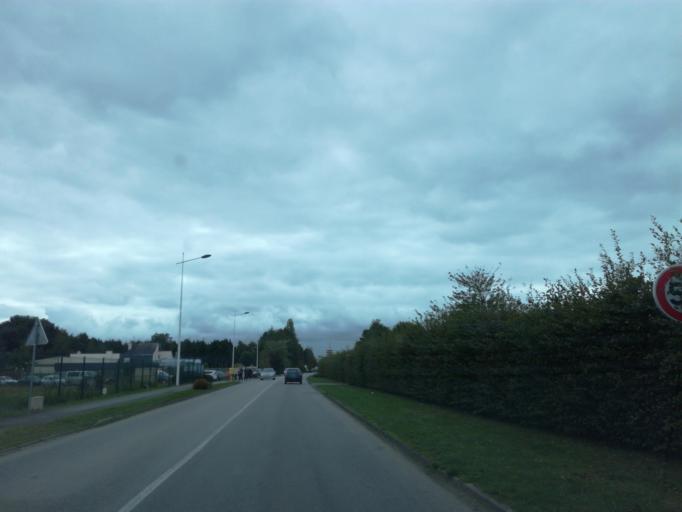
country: FR
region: Brittany
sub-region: Departement des Cotes-d'Armor
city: Loudeac
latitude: 48.1599
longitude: -2.7551
